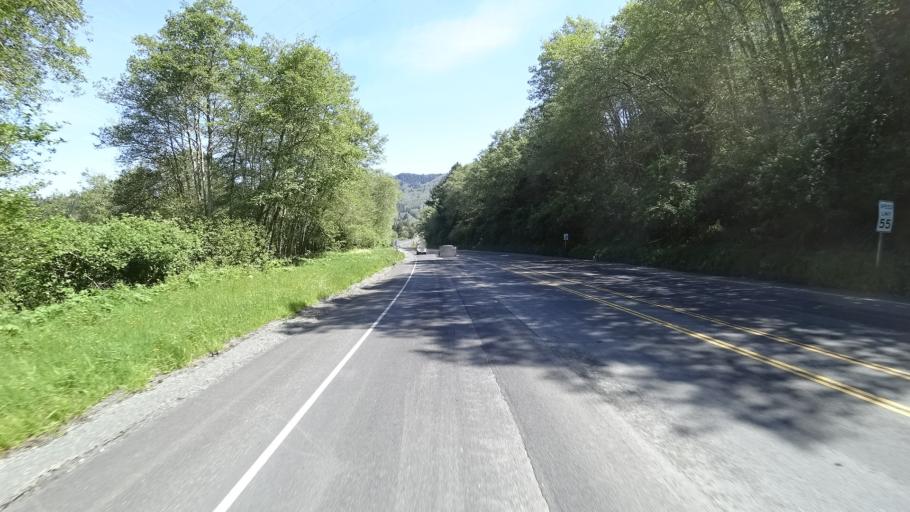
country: US
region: California
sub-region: Humboldt County
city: Westhaven-Moonstone
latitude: 41.2207
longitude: -124.0969
